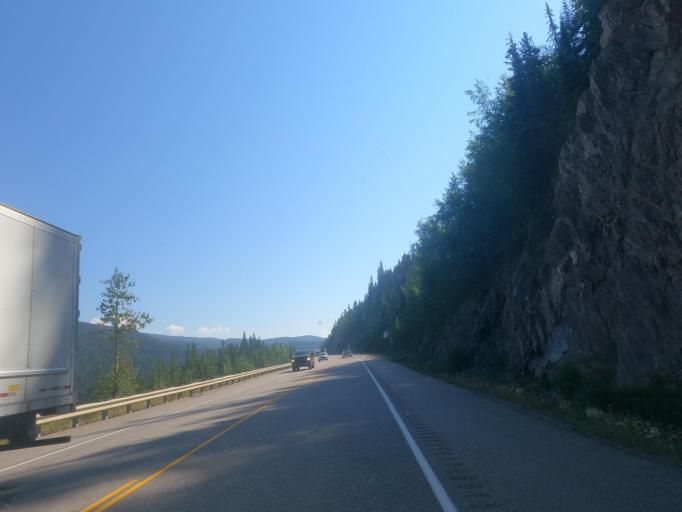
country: CA
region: Alberta
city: Jasper Park Lodge
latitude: 52.8726
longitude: -118.2948
